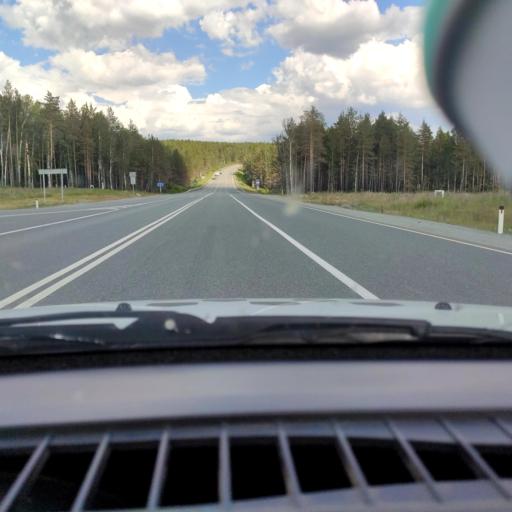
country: RU
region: Chelyabinsk
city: Zlatoust
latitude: 55.0556
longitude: 59.6973
